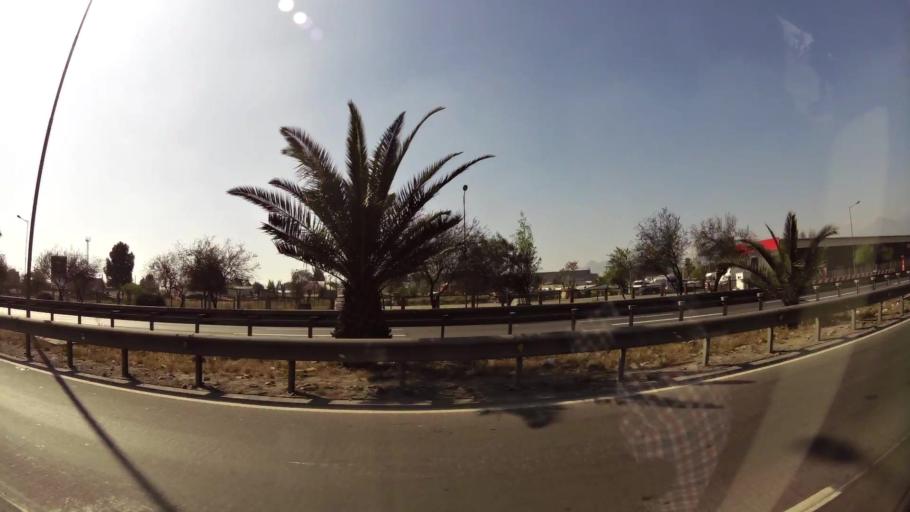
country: CL
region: Santiago Metropolitan
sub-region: Provincia de Santiago
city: Lo Prado
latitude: -33.3724
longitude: -70.7320
